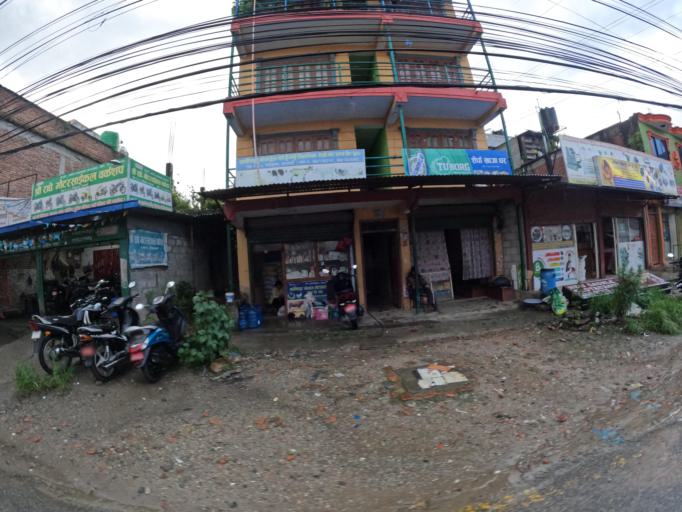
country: NP
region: Central Region
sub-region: Bagmati Zone
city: Kathmandu
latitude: 27.7615
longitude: 85.3301
